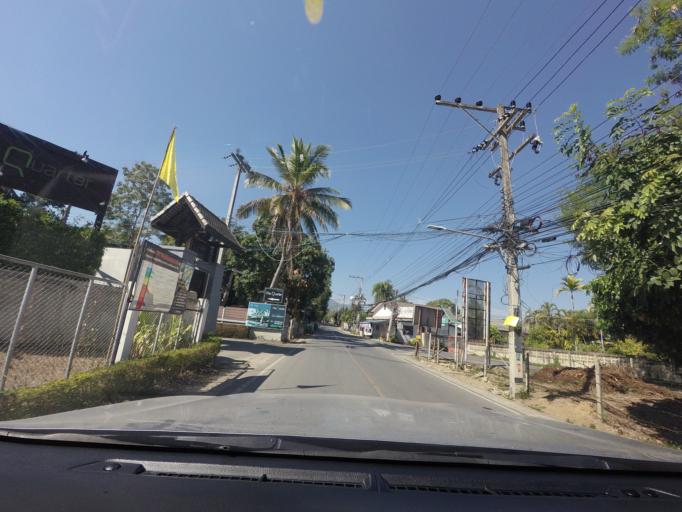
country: TH
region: Chiang Mai
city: Pai
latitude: 19.3622
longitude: 98.4369
